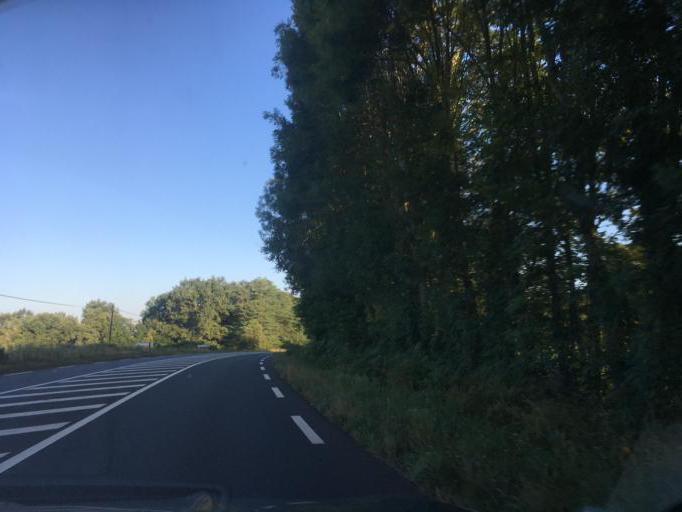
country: FR
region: Aquitaine
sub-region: Departement des Pyrenees-Atlantiques
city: Ger
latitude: 43.2478
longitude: -0.1078
